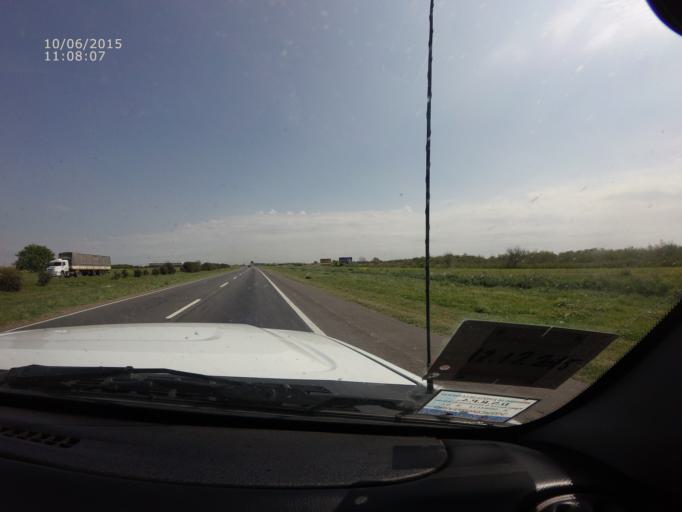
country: AR
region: Santa Fe
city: Arroyo Seco
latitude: -33.1801
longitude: -60.5159
